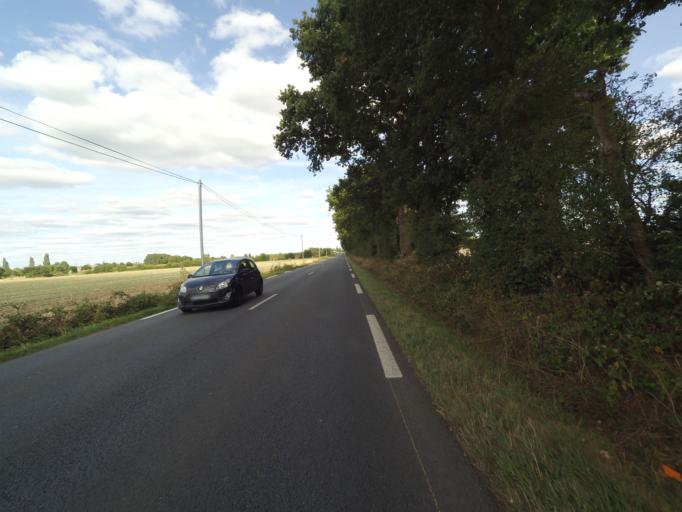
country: FR
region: Pays de la Loire
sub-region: Departement de la Loire-Atlantique
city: Vieillevigne
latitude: 46.9722
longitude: -1.3950
